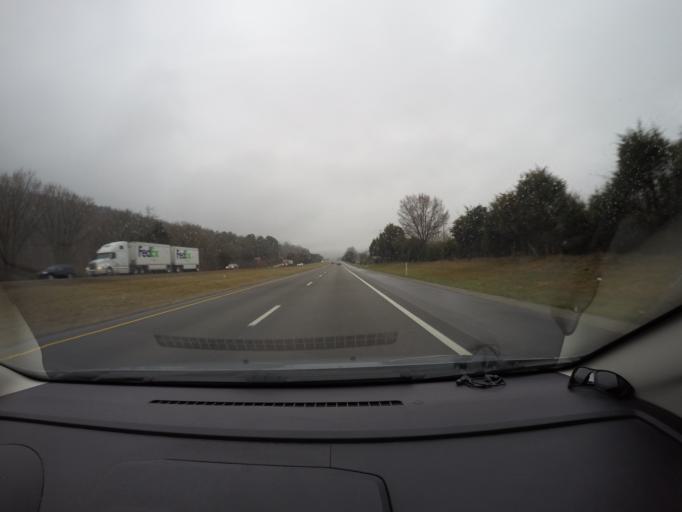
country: US
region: Tennessee
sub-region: Marion County
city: Kimball
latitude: 35.0970
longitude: -85.7372
